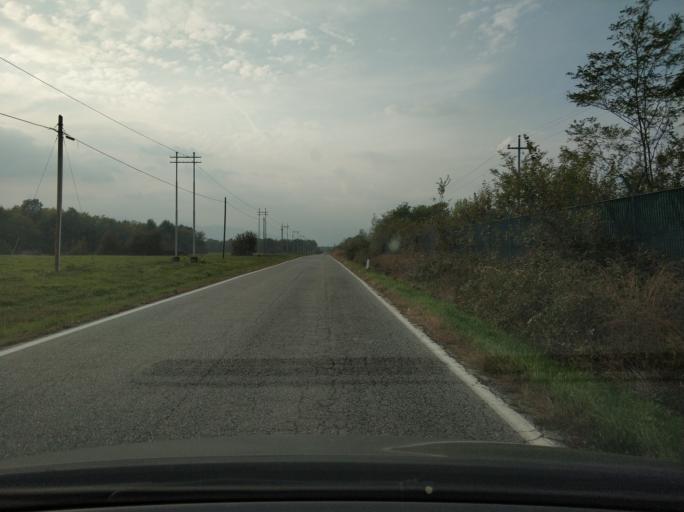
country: IT
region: Piedmont
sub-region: Provincia di Torino
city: San Francesco al Campo
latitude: 45.2443
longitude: 7.6679
